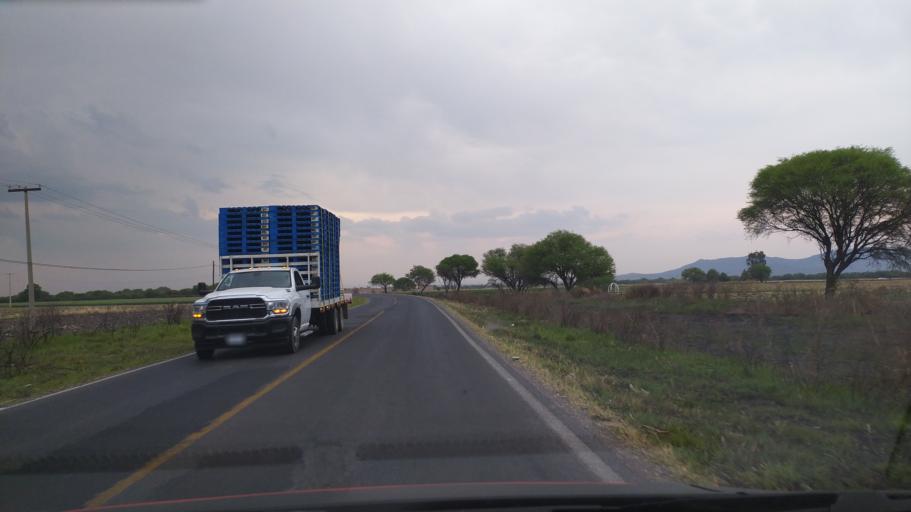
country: MX
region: Guanajuato
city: Ciudad Manuel Doblado
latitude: 20.7605
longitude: -101.9168
